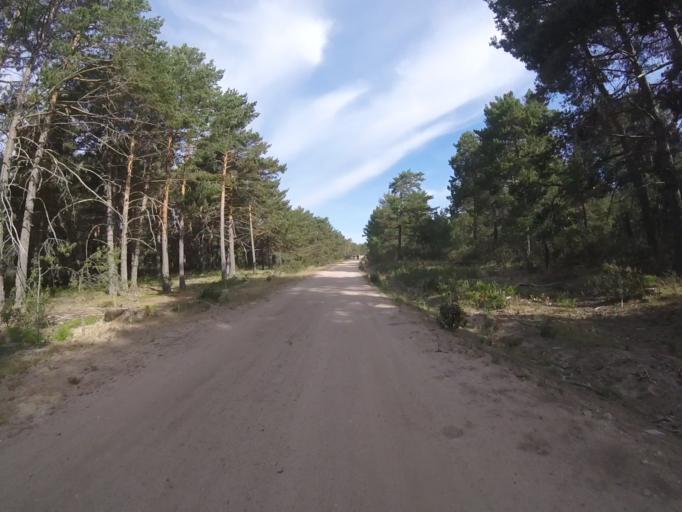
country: ES
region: Castille and Leon
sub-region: Provincia de Avila
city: Peguerinos
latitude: 40.6521
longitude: -4.1803
